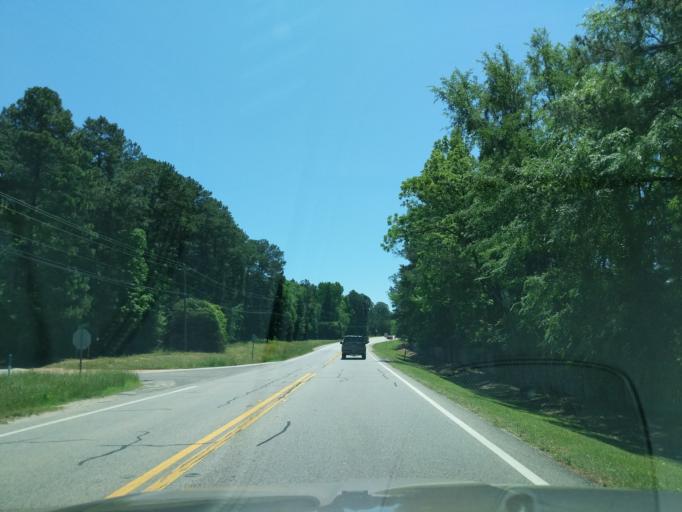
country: US
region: Georgia
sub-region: Columbia County
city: Evans
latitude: 33.5556
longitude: -82.0948
